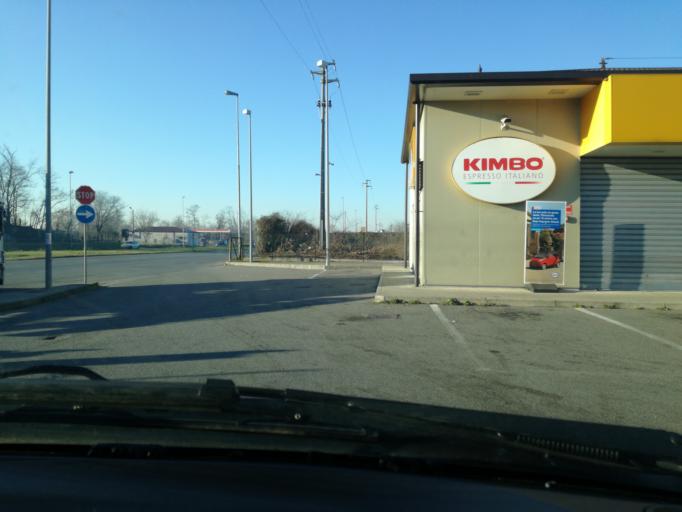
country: IT
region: Lombardy
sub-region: Provincia di Monza e Brianza
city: Brugherio
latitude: 45.5698
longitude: 9.2939
